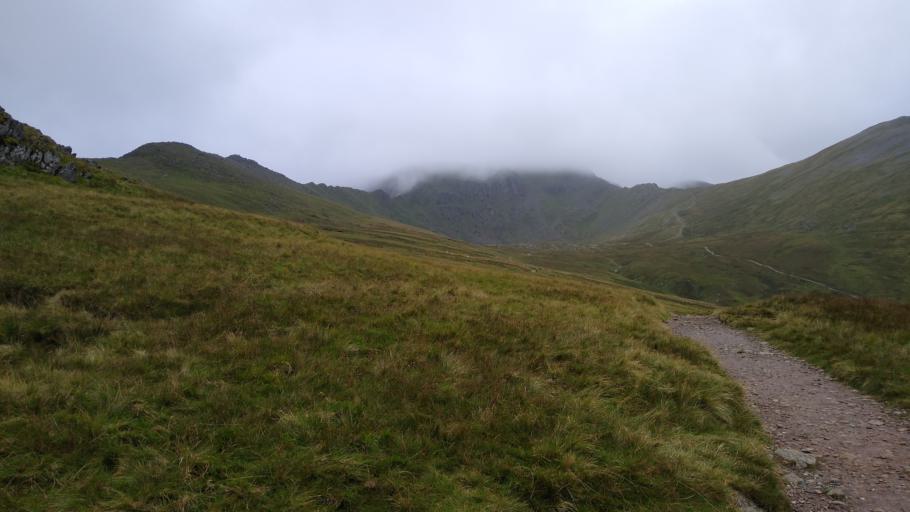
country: GB
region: England
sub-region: Cumbria
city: Ambleside
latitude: 54.5311
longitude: -2.9916
